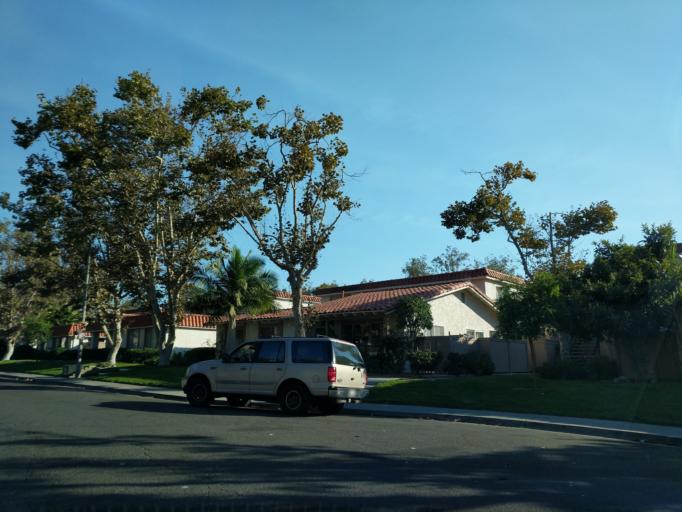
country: US
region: California
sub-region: Orange County
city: San Juan Capistrano
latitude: 33.5086
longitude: -117.6672
